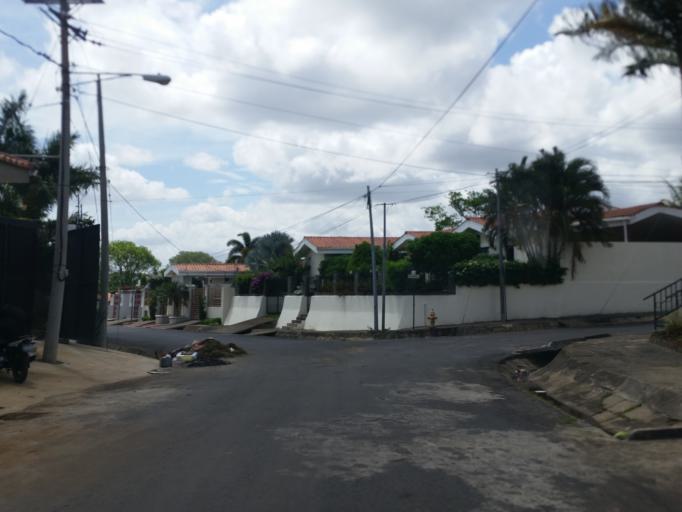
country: NI
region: Managua
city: Managua
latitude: 12.0765
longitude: -86.2369
